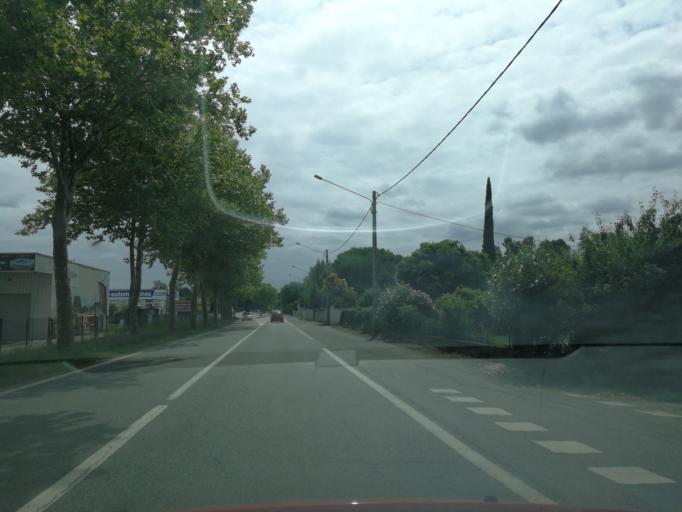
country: FR
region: Midi-Pyrenees
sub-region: Departement de la Haute-Garonne
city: Balma
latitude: 43.5853
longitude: 1.5143
